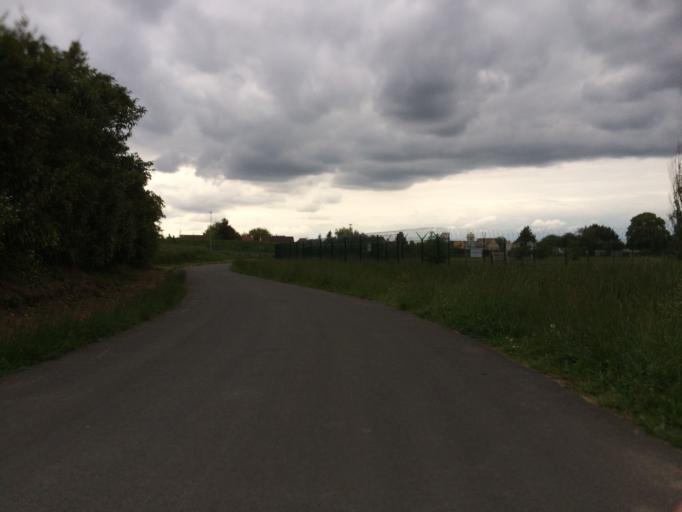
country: FR
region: Ile-de-France
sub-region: Departement de l'Essonne
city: Le Plessis-Pate
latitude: 48.6046
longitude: 2.3231
